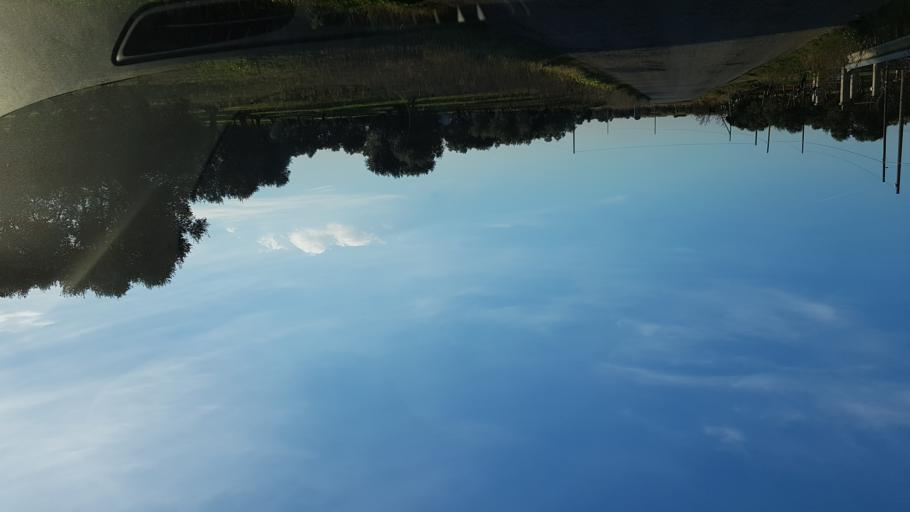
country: IT
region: Apulia
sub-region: Provincia di Brindisi
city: San Vito dei Normanni
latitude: 40.6681
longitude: 17.7797
